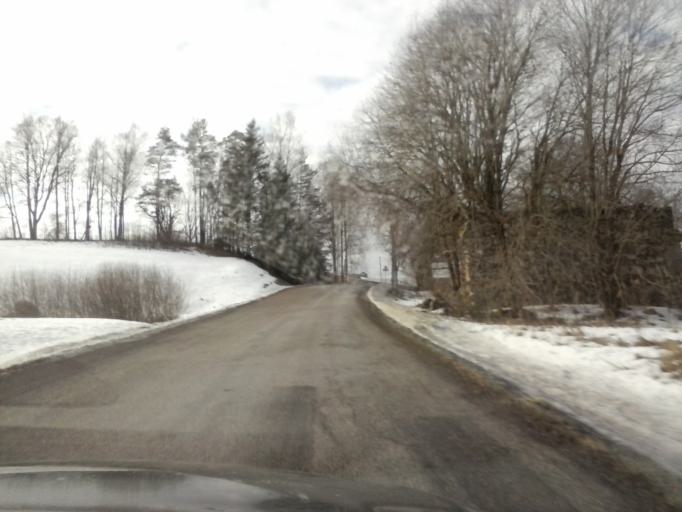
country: EE
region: Tartu
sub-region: Elva linn
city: Elva
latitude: 58.0301
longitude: 26.3498
